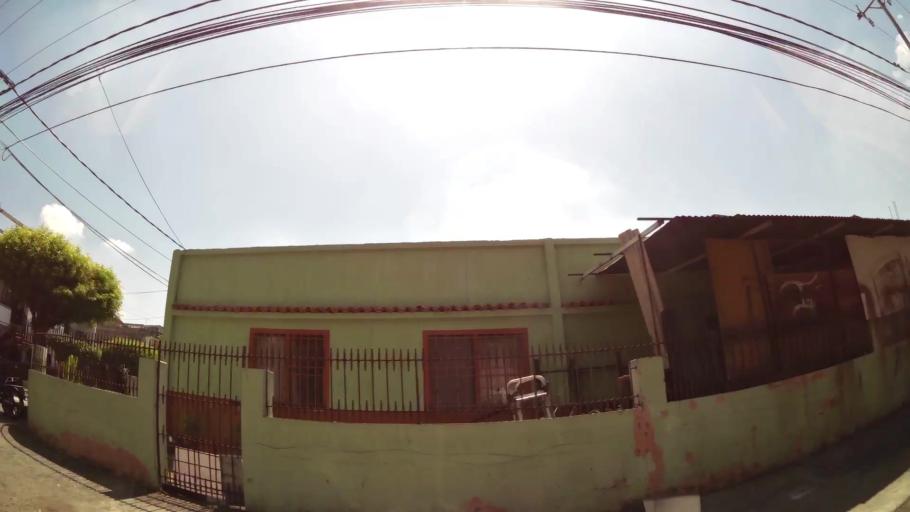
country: CO
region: Valle del Cauca
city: Cali
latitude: 3.4326
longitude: -76.4987
